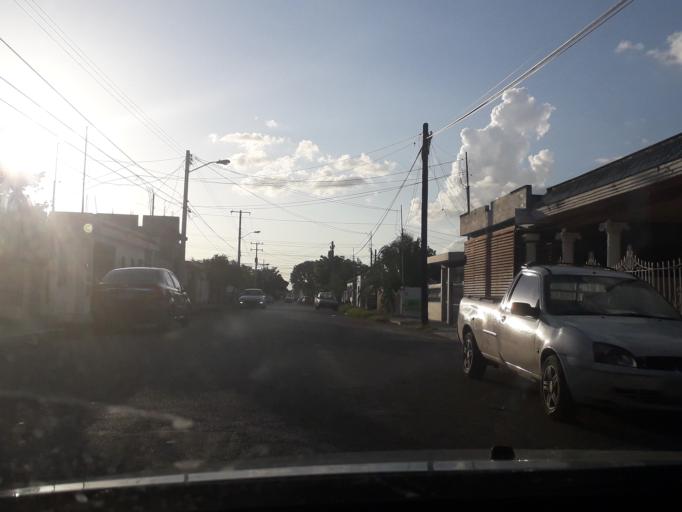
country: MX
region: Yucatan
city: Merida
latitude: 20.9804
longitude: -89.6531
